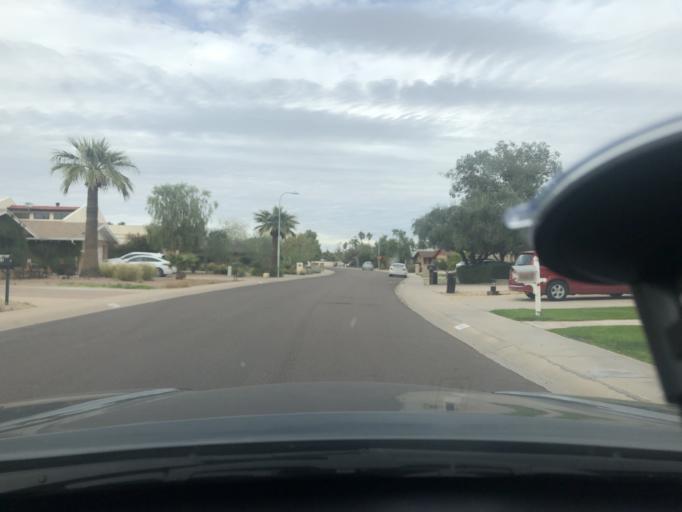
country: US
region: Arizona
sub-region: Maricopa County
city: Scottsdale
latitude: 33.4822
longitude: -111.9041
